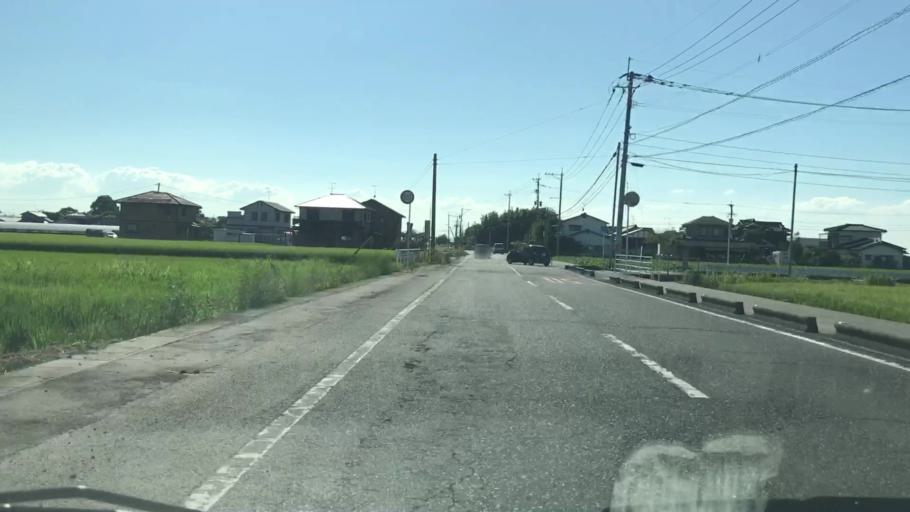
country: JP
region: Saga Prefecture
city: Okawa
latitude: 33.2201
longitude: 130.3431
